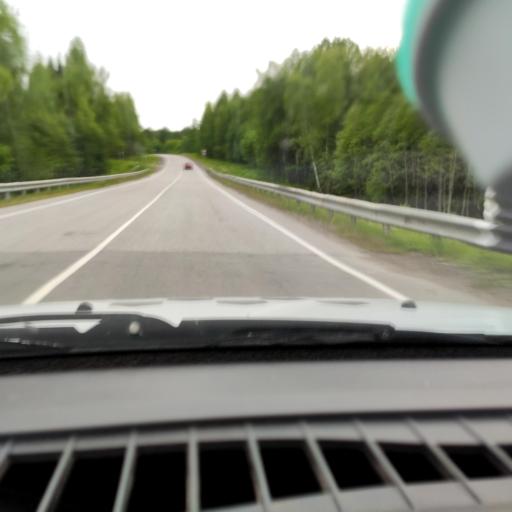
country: RU
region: Perm
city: Lys'va
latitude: 58.1541
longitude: 57.7671
